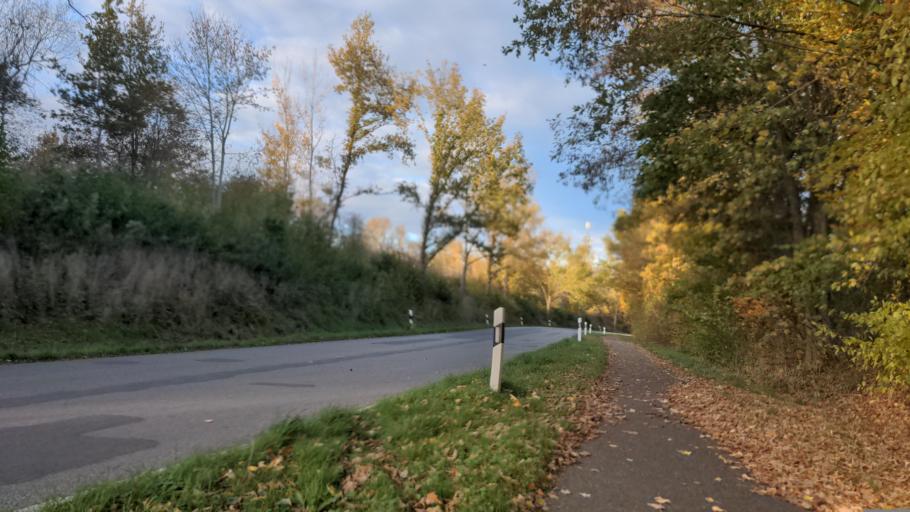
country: DE
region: Schleswig-Holstein
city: Heidekamp
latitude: 53.8597
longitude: 10.5012
